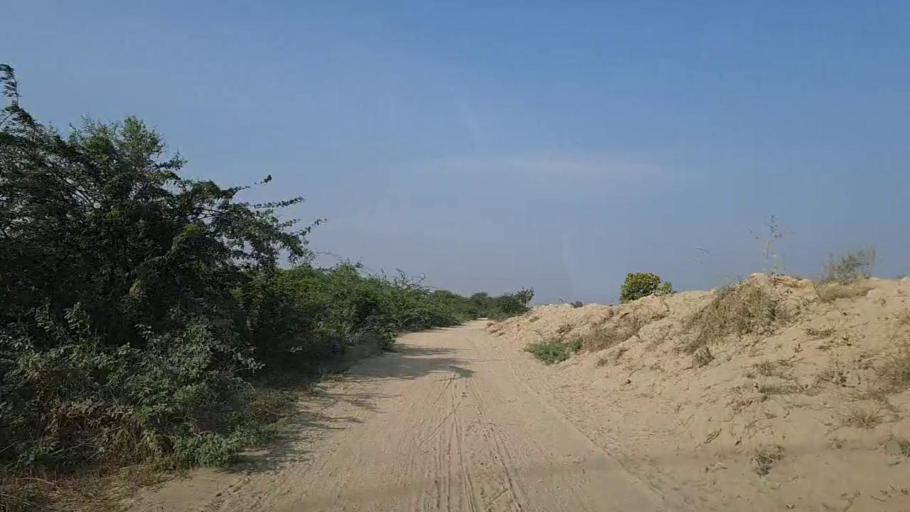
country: PK
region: Sindh
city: Mirpur Sakro
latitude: 24.5957
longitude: 67.6486
